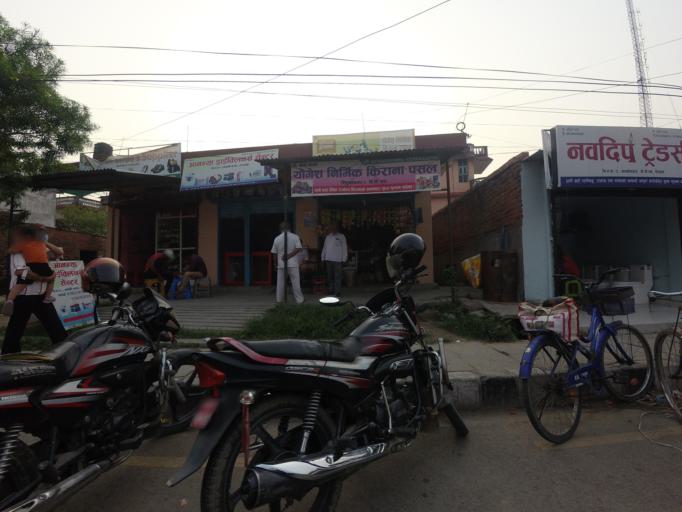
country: NP
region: Western Region
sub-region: Lumbini Zone
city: Bhairahawa
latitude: 27.5159
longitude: 83.4491
